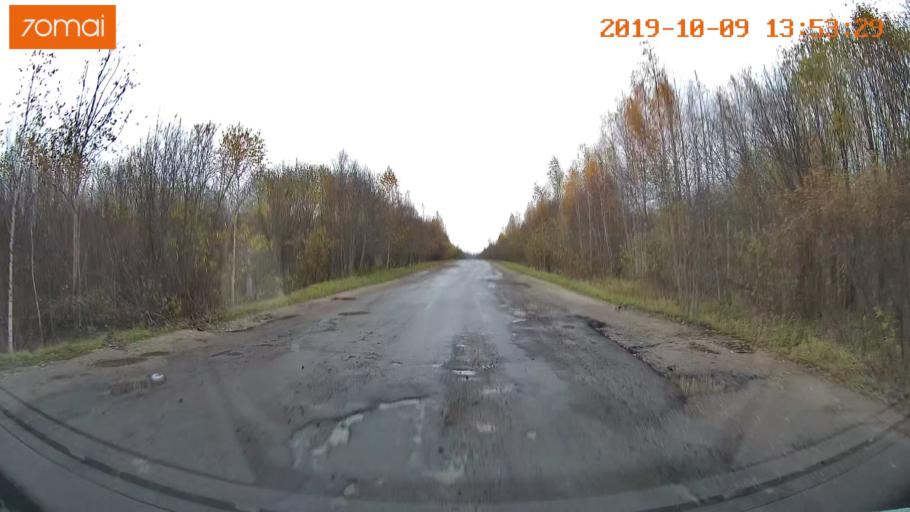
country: RU
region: Kostroma
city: Buy
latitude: 58.4157
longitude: 41.2585
